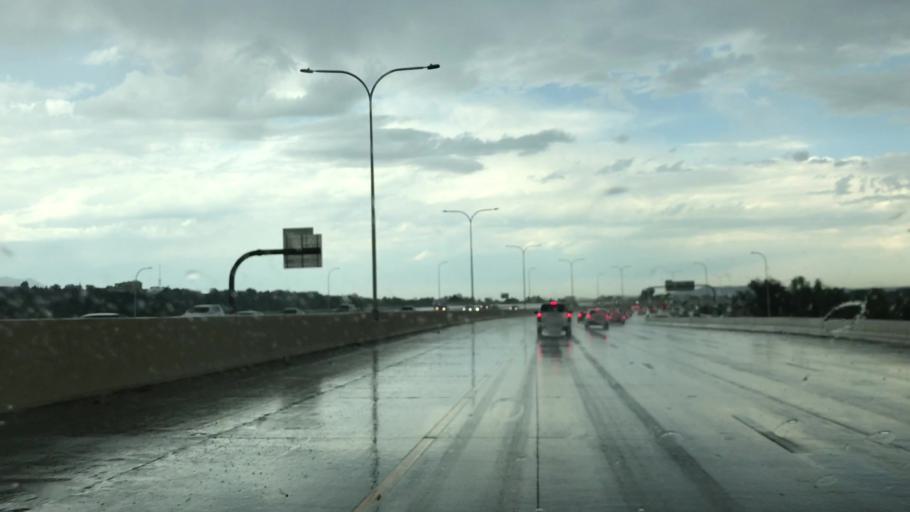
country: US
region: Colorado
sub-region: El Paso County
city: Colorado Springs
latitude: 38.8290
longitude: -104.8350
